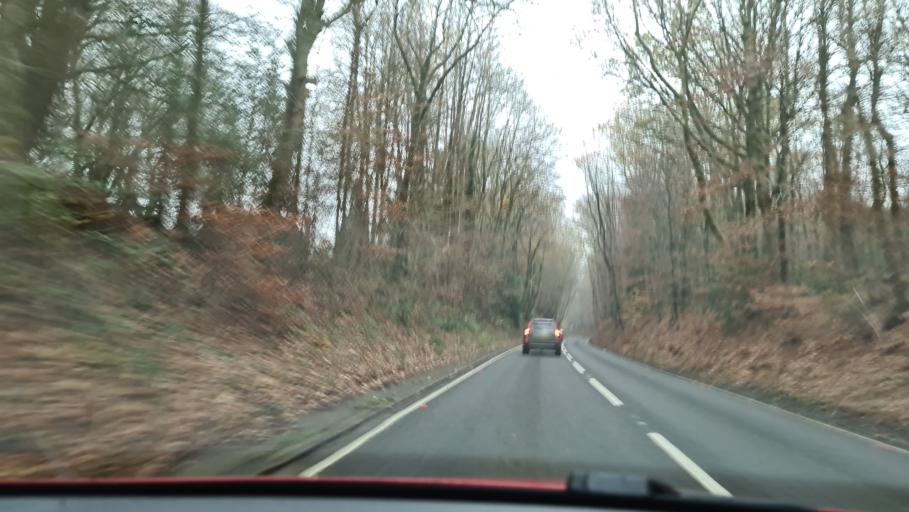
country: GB
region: England
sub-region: Buckinghamshire
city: Stokenchurch
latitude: 51.6479
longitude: -0.8552
